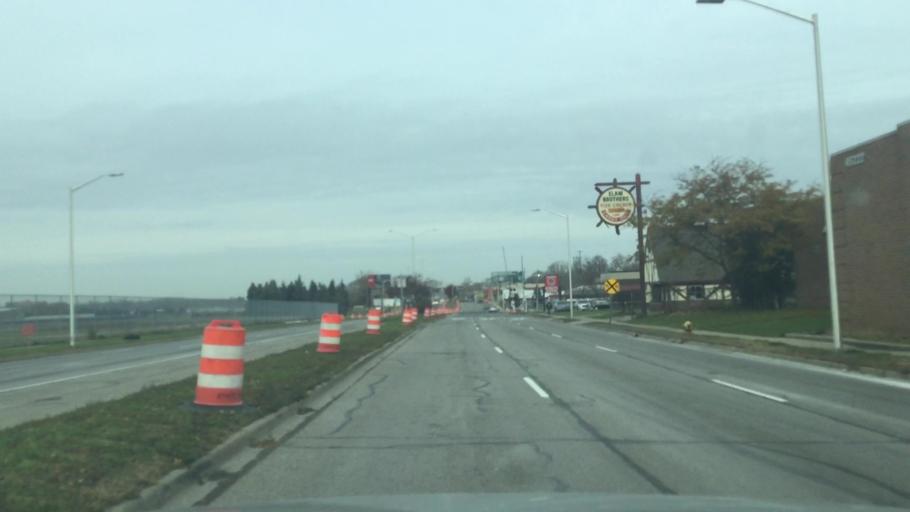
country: US
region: Michigan
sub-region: Oakland County
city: Pontiac
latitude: 42.6211
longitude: -83.2805
